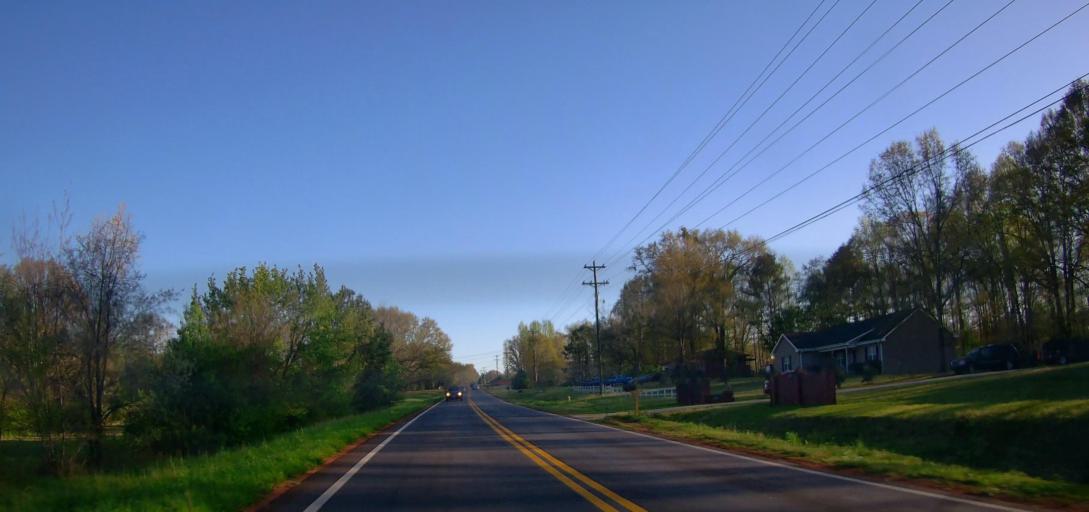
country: US
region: Georgia
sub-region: Newton County
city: Porterdale
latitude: 33.5750
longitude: -83.9046
